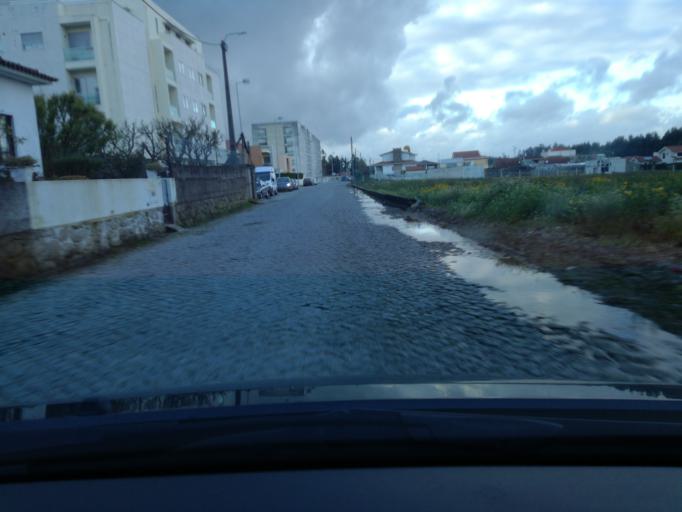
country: PT
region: Porto
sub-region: Maia
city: Gemunde
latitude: 41.2595
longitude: -8.6625
